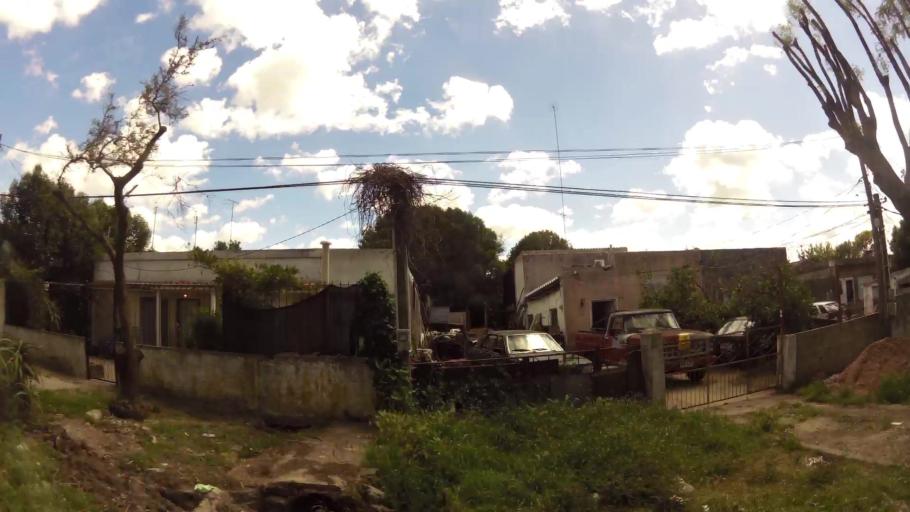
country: UY
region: Canelones
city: Paso de Carrasco
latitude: -34.8374
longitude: -56.1149
